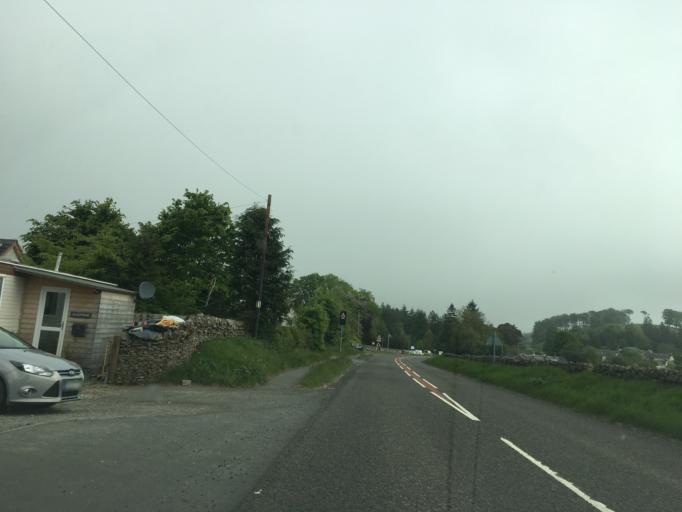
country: GB
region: Scotland
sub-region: The Scottish Borders
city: West Linton
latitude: 55.7164
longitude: -3.3430
